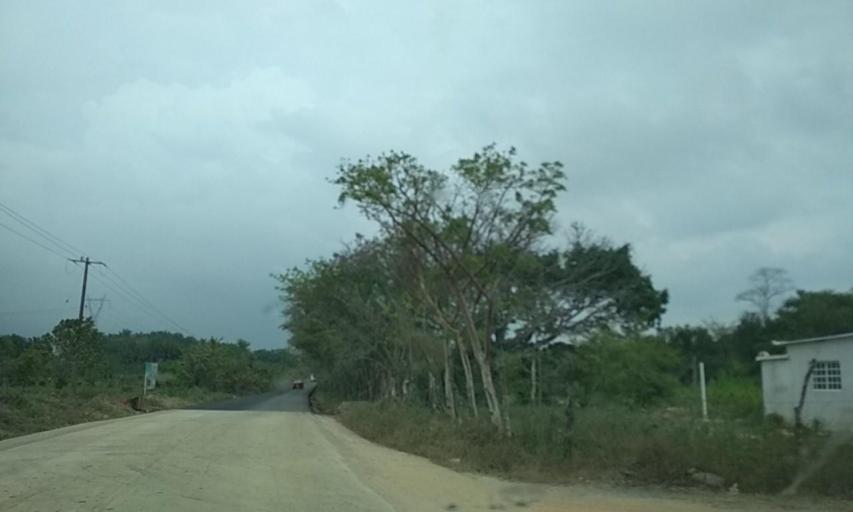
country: MX
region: Tabasco
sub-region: Huimanguillo
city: Francisco Rueda
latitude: 17.7196
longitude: -94.0952
